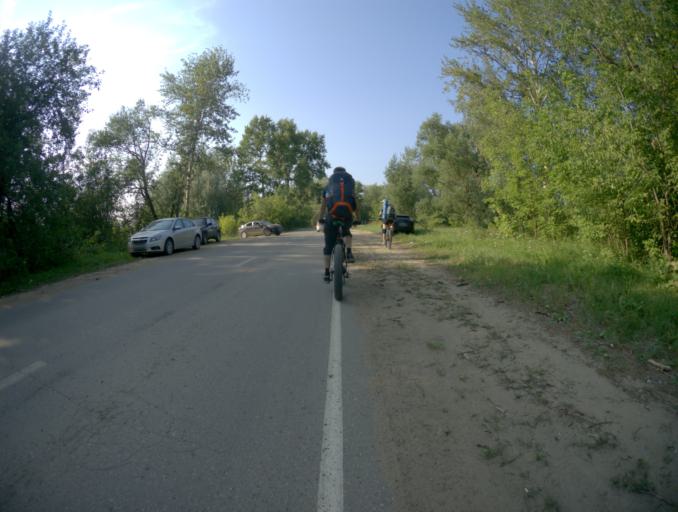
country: RU
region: Nizjnij Novgorod
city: Bor
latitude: 56.3523
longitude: 44.0519
